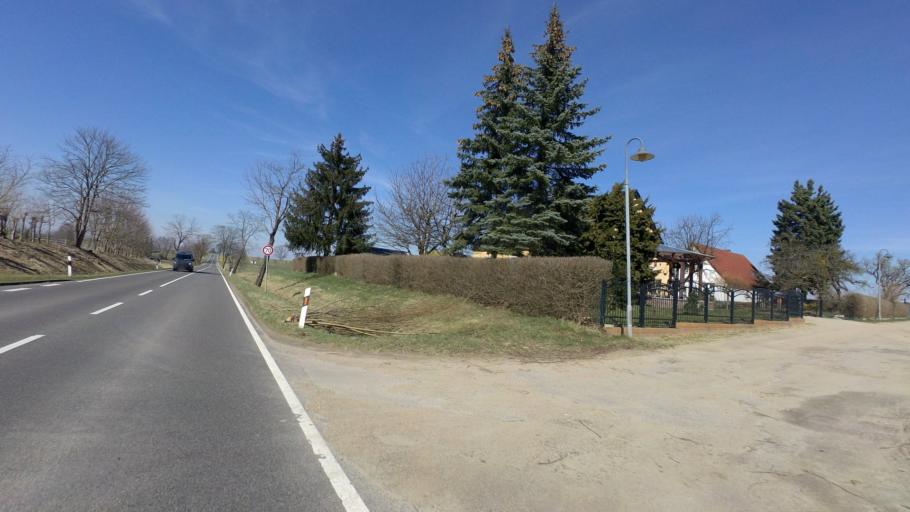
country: DE
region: Brandenburg
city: Protzel
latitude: 52.6015
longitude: 14.0242
